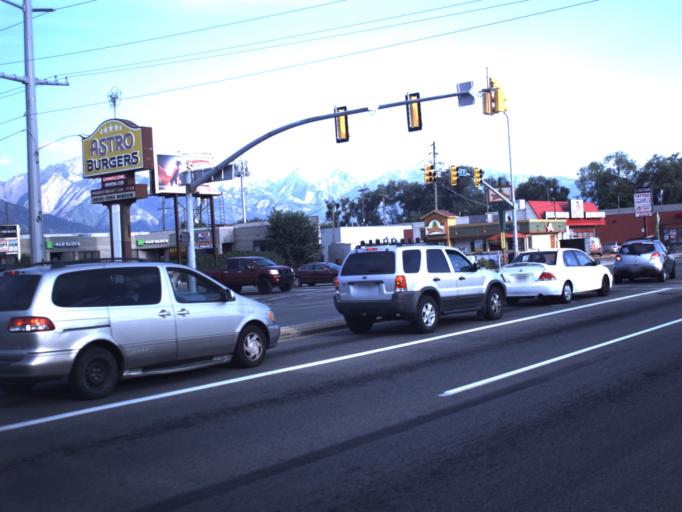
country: US
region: Utah
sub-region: Salt Lake County
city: Centerfield
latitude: 40.6874
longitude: -111.8884
